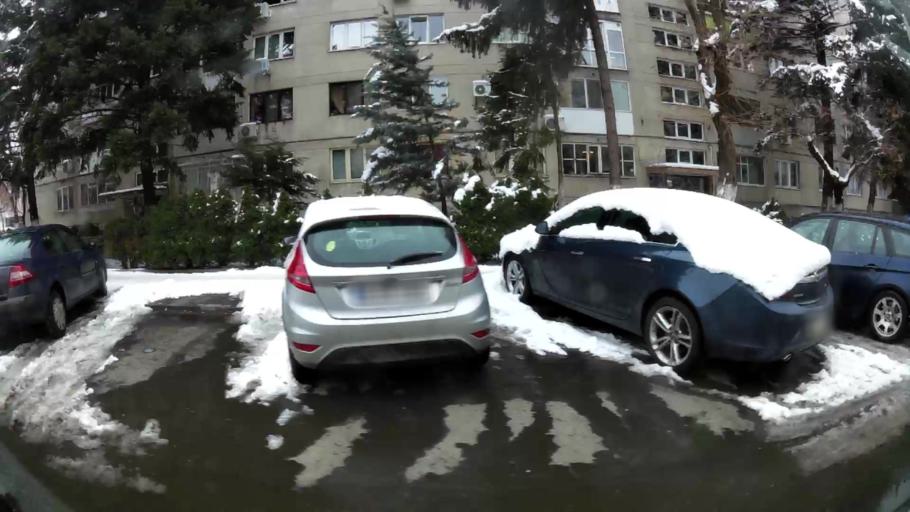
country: RO
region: Bucuresti
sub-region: Municipiul Bucuresti
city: Bucuresti
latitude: 44.3920
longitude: 26.1159
